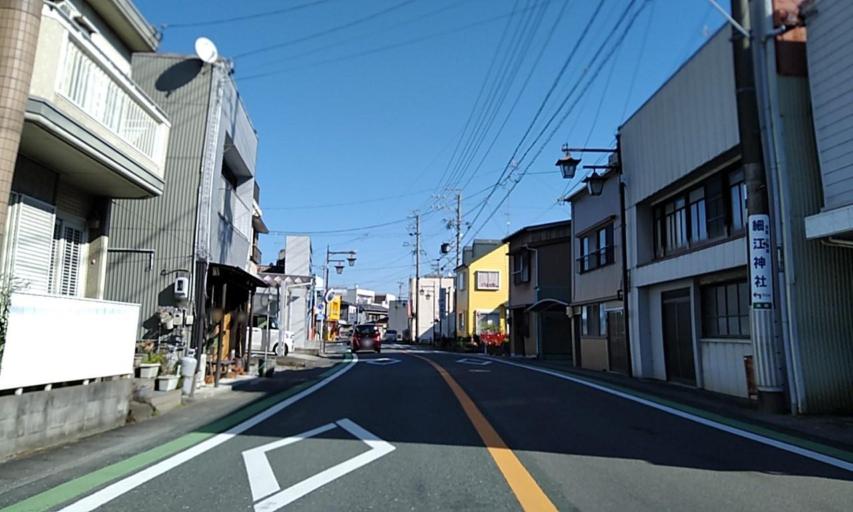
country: JP
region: Shizuoka
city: Hamakita
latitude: 34.8095
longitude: 137.6524
